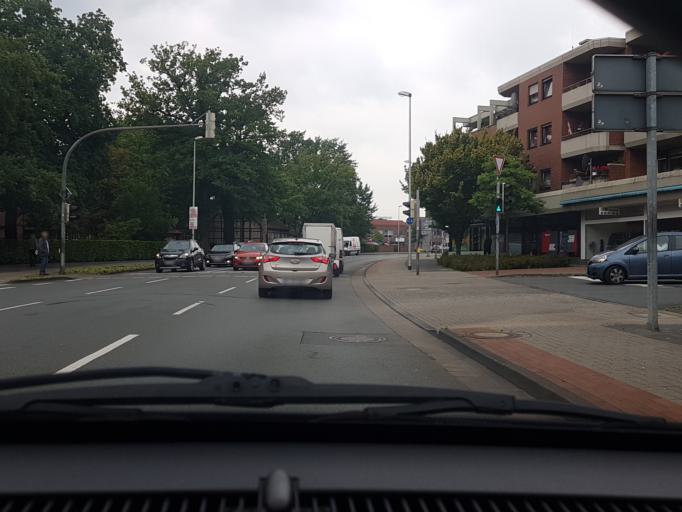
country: DE
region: North Rhine-Westphalia
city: Emsdetten
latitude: 52.1733
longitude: 7.5314
